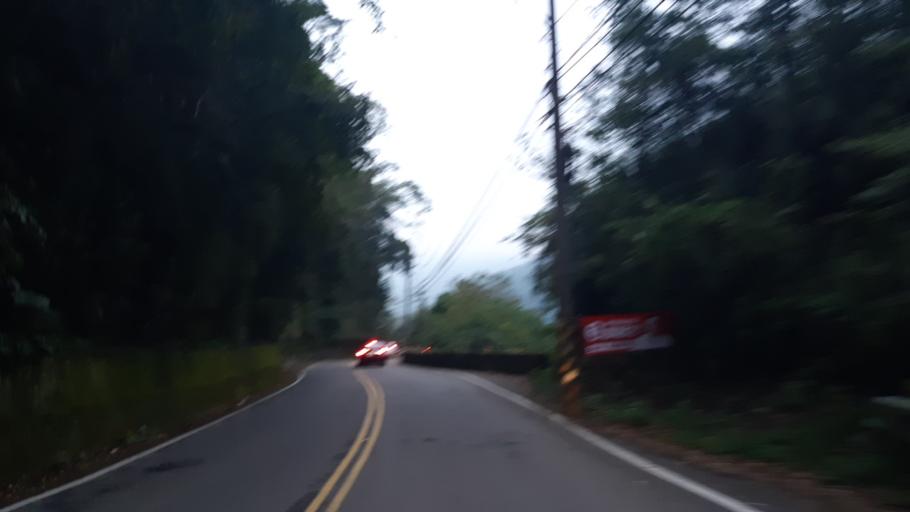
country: TW
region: Taiwan
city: Daxi
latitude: 24.6990
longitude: 121.2179
